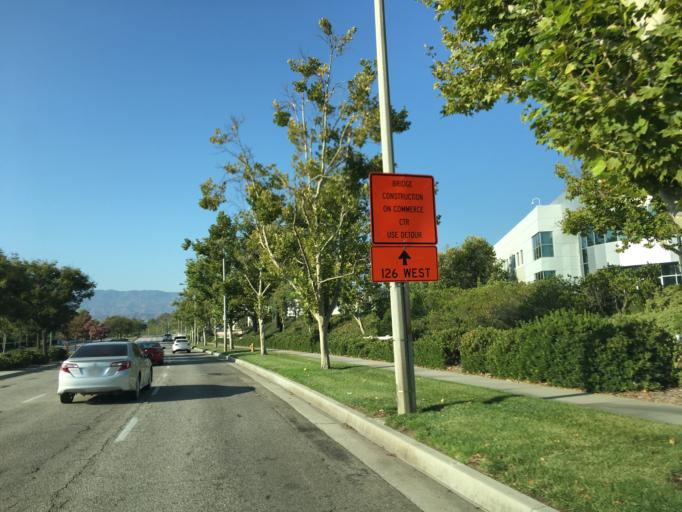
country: US
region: California
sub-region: Los Angeles County
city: Valencia
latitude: 34.4492
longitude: -118.6262
